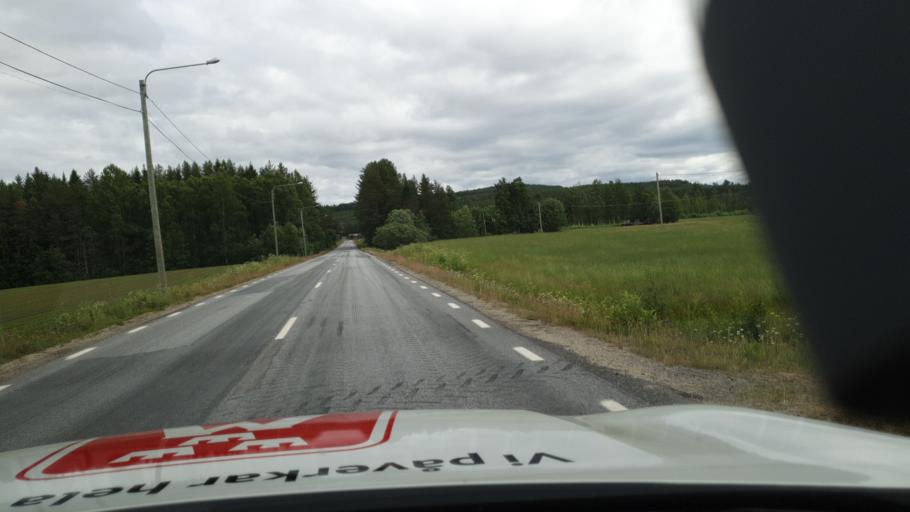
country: SE
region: Vaesterbotten
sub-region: Vannas Kommun
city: Vaennaes
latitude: 63.8944
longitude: 19.7109
